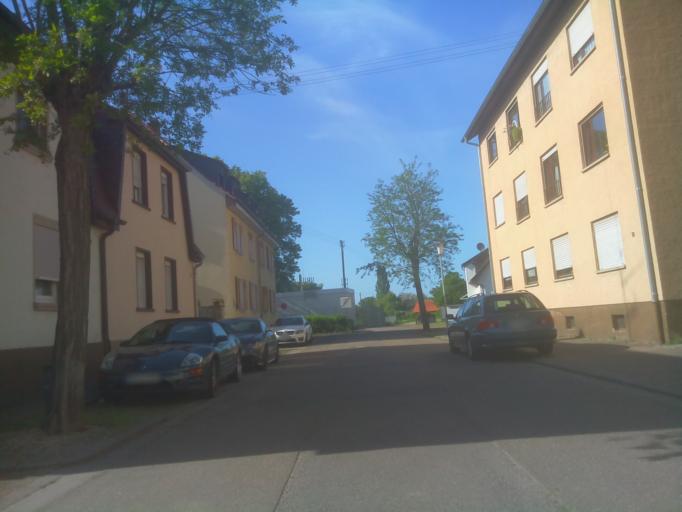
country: DE
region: Baden-Wuerttemberg
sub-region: Karlsruhe Region
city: Ladenburg
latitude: 49.4770
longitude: 8.6095
